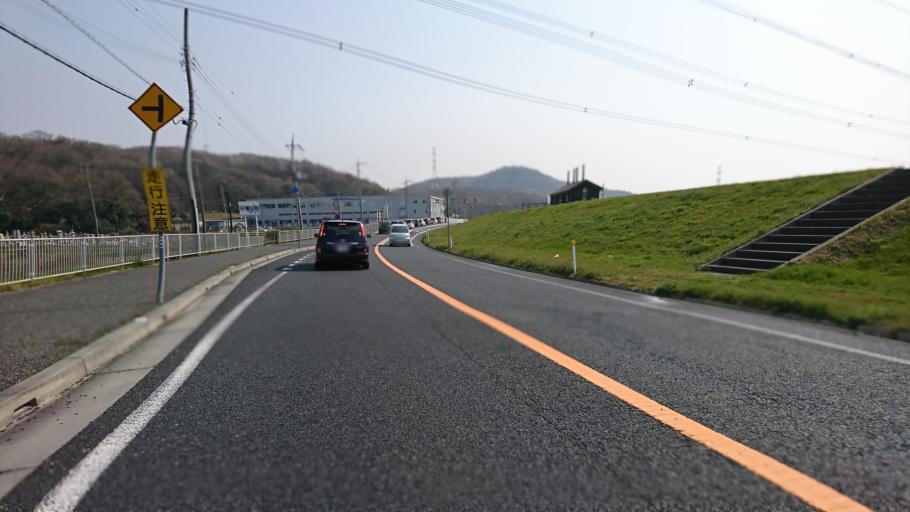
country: JP
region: Hyogo
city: Ono
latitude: 34.8195
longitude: 134.9387
